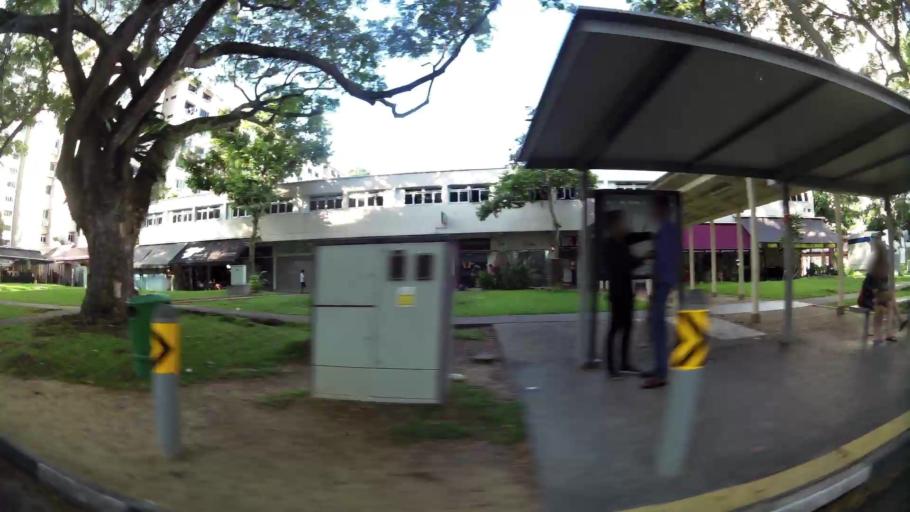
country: SG
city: Singapore
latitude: 1.3200
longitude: 103.9442
